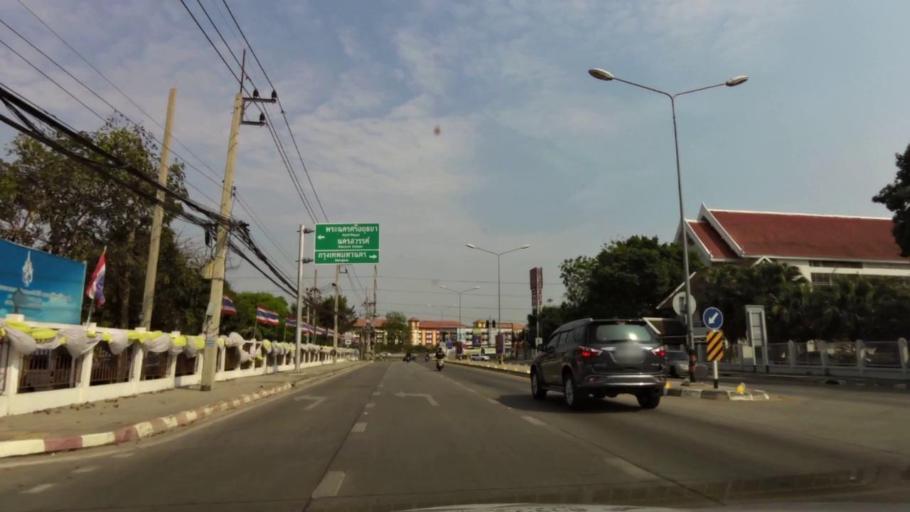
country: TH
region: Phra Nakhon Si Ayutthaya
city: Phra Nakhon Si Ayutthaya
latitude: 14.3333
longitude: 100.6119
